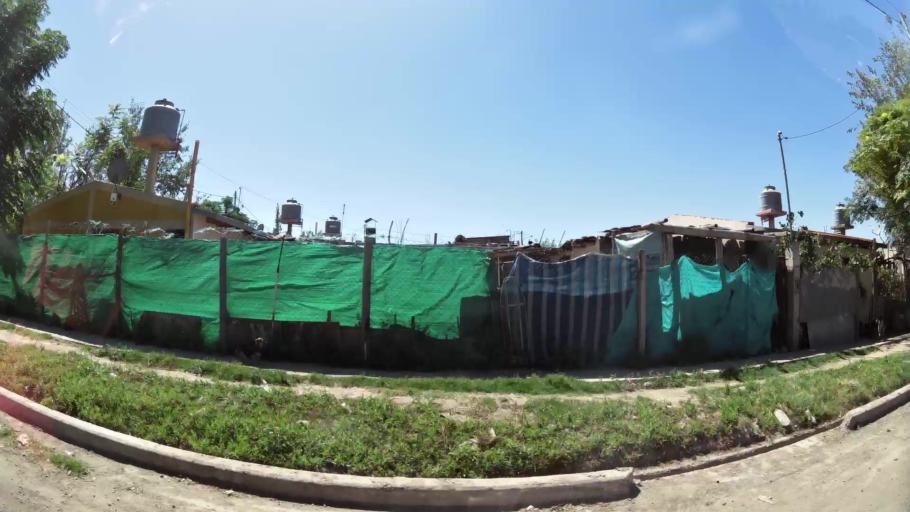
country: AR
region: Mendoza
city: Villa Nueva
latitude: -32.8743
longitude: -68.7858
